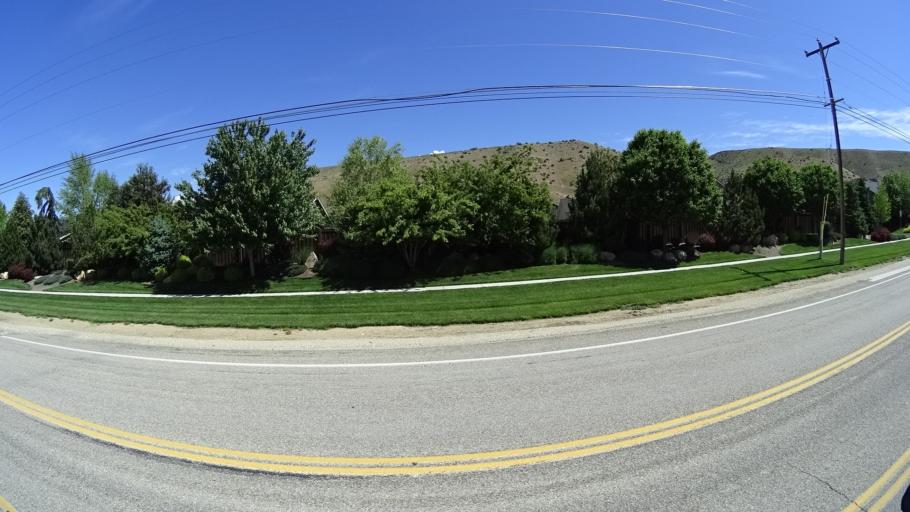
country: US
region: Idaho
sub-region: Ada County
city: Boise
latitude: 43.5628
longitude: -116.1071
